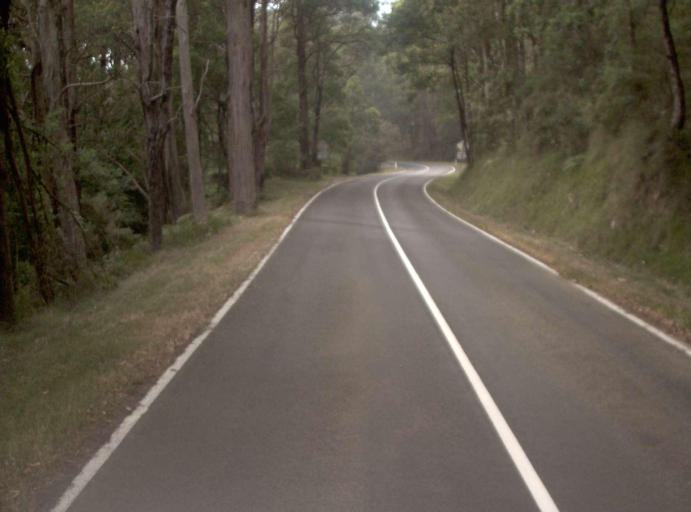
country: AU
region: Victoria
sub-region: Yarra Ranges
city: Badger Creek
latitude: -37.7004
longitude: 145.5677
